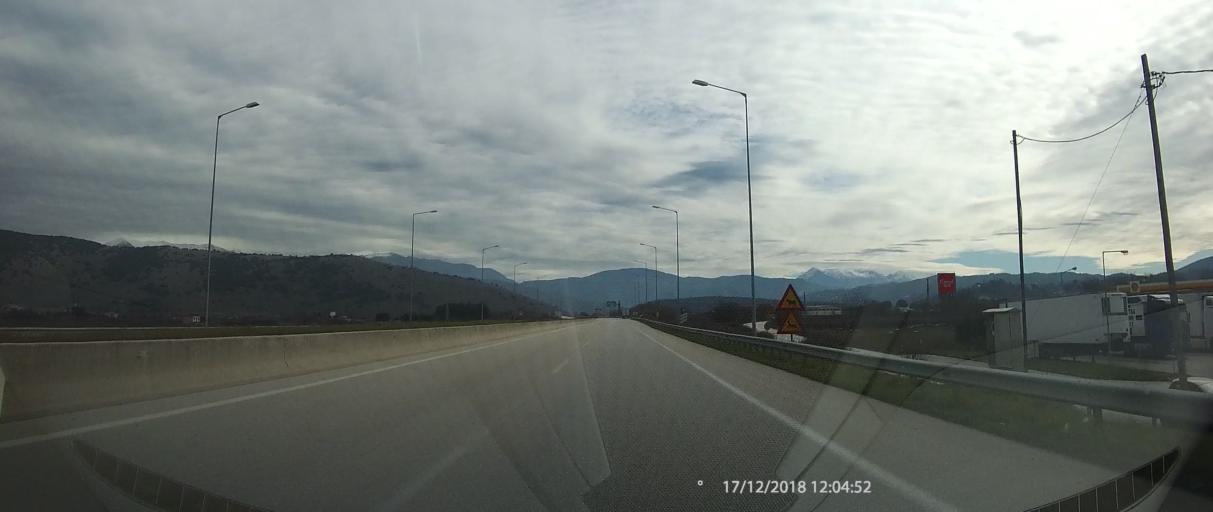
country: GR
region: Epirus
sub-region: Nomos Ioanninon
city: Koutselio
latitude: 39.6016
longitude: 20.8958
